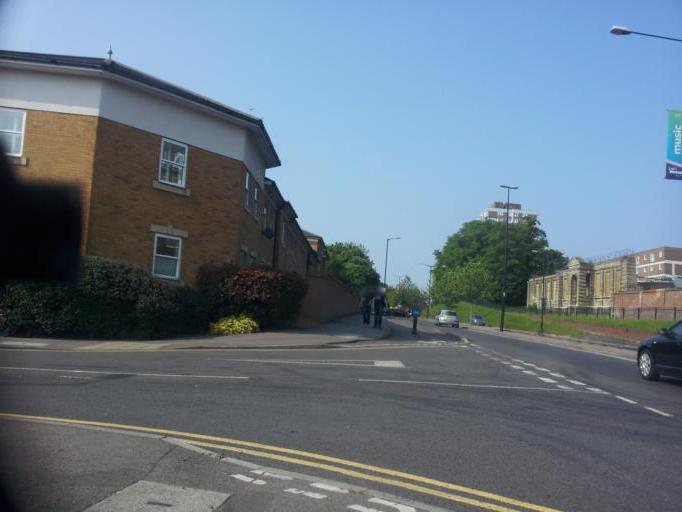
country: GB
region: England
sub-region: Kent
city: Chatham
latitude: 51.3894
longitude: 0.5255
